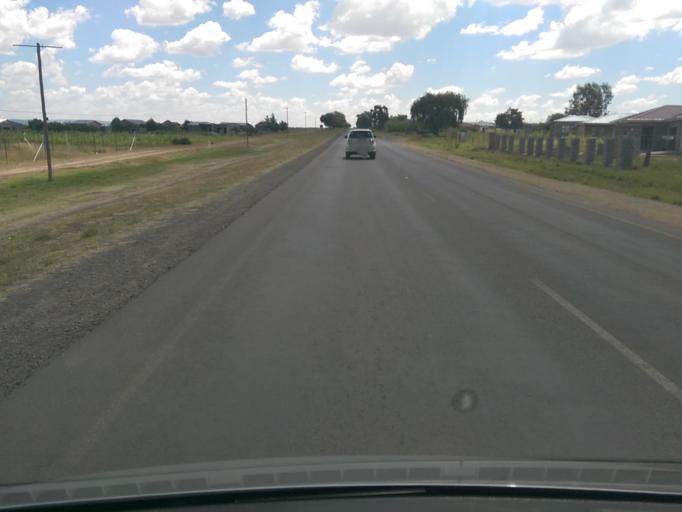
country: LS
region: Maseru
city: Maseru
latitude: -29.4102
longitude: 27.6164
